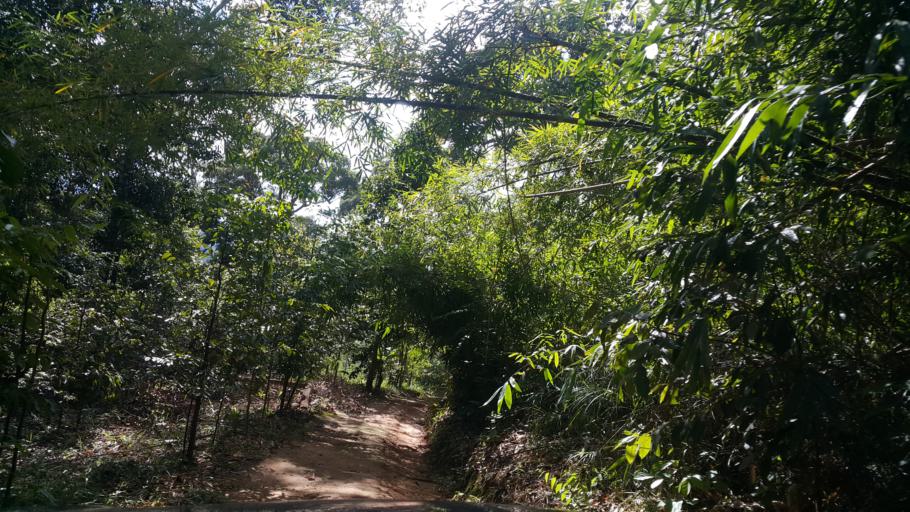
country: TH
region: Loei
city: Na Haeo
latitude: 17.5536
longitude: 100.9567
